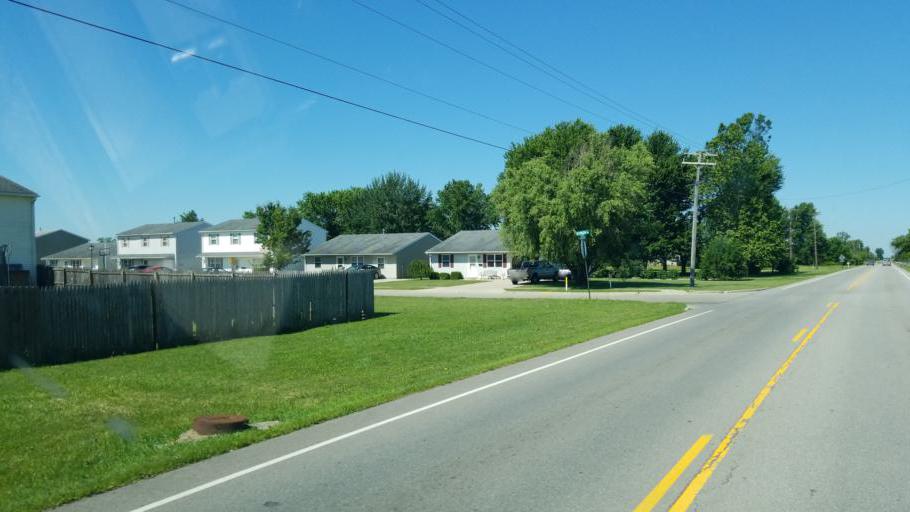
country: US
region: Ohio
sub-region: Marion County
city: Marion
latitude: 40.6149
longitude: -83.1120
